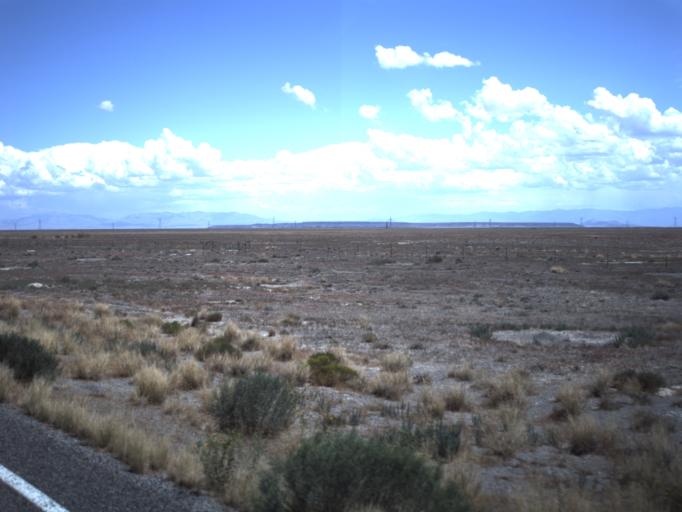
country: US
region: Utah
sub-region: Millard County
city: Delta
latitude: 39.2219
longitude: -112.9464
